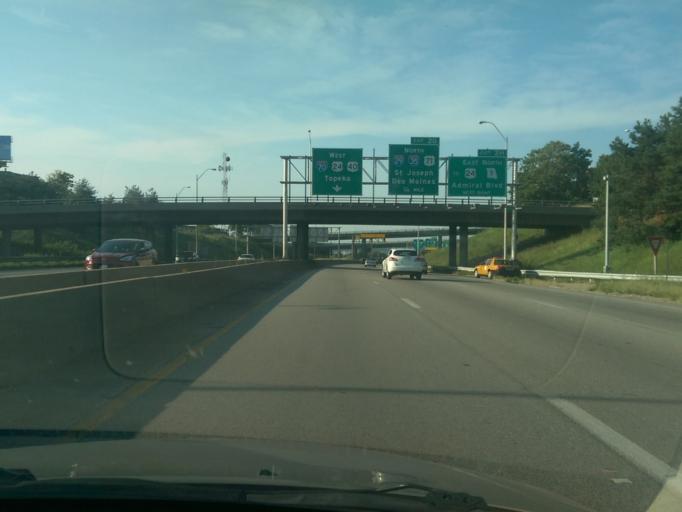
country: US
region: Missouri
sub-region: Jackson County
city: Kansas City
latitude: 39.1014
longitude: -94.5725
